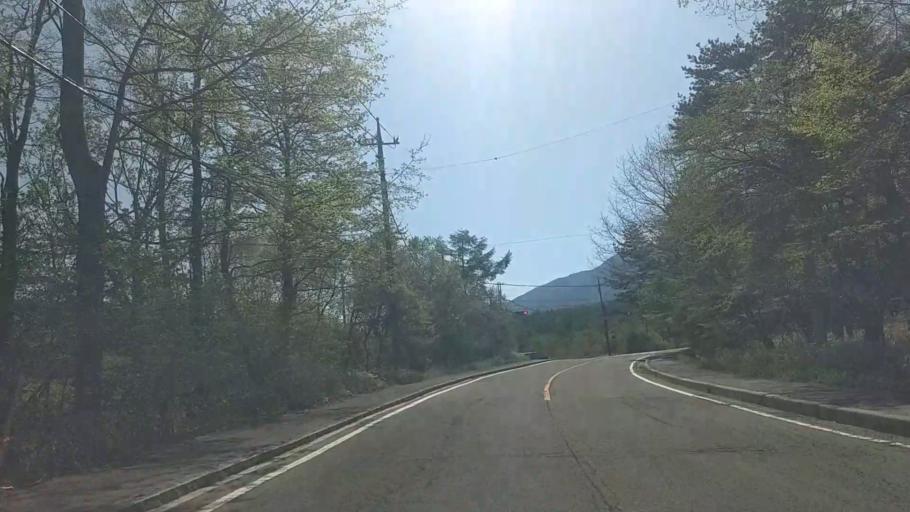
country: JP
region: Yamanashi
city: Nirasaki
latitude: 35.9351
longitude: 138.4256
